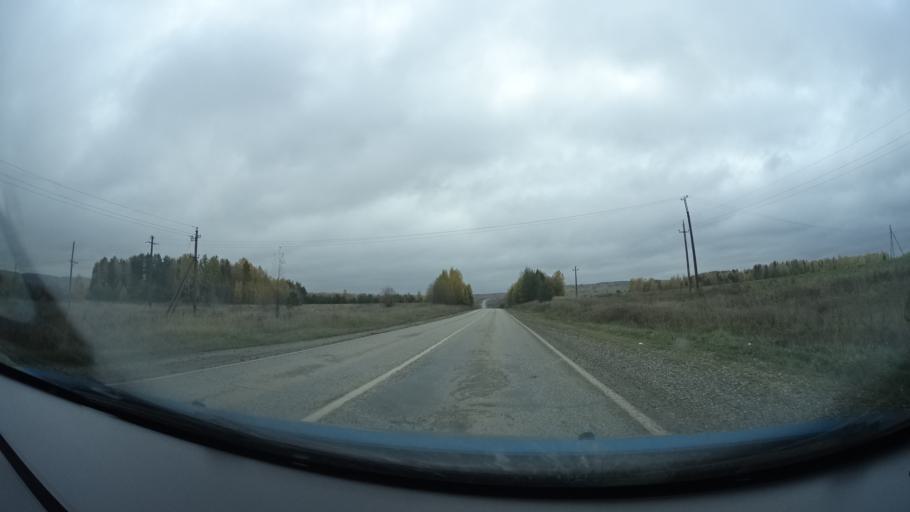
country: RU
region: Perm
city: Osa
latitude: 57.1536
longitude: 55.5296
